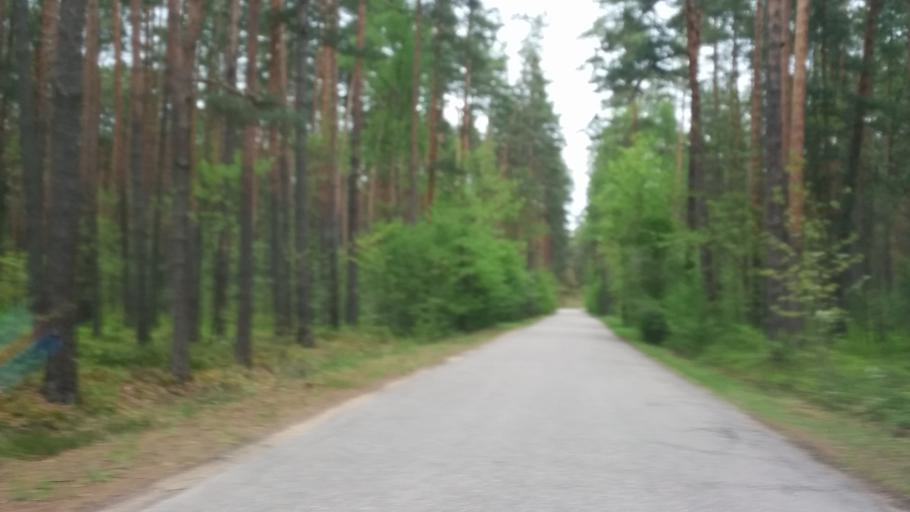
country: LV
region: Babite
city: Pinki
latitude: 56.9387
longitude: 23.9345
